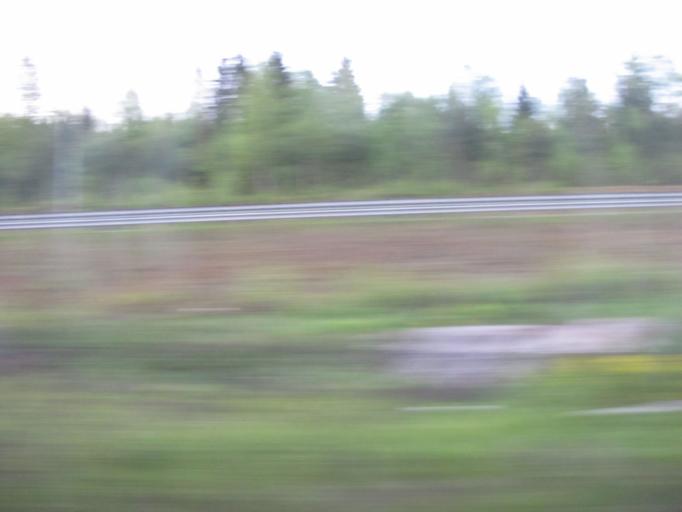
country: NO
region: Oppland
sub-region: Lillehammer
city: Lillehammer
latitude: 61.2001
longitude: 10.4189
